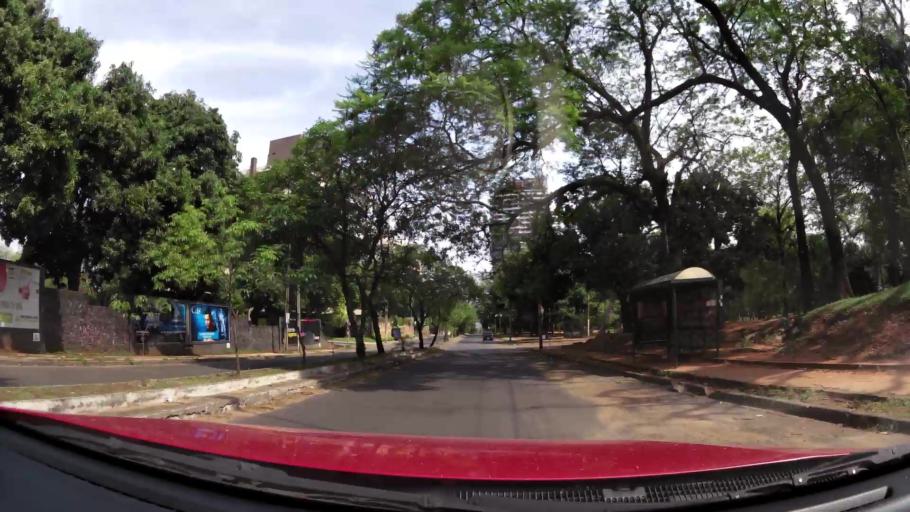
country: PY
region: Asuncion
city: Asuncion
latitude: -25.2642
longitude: -57.5718
